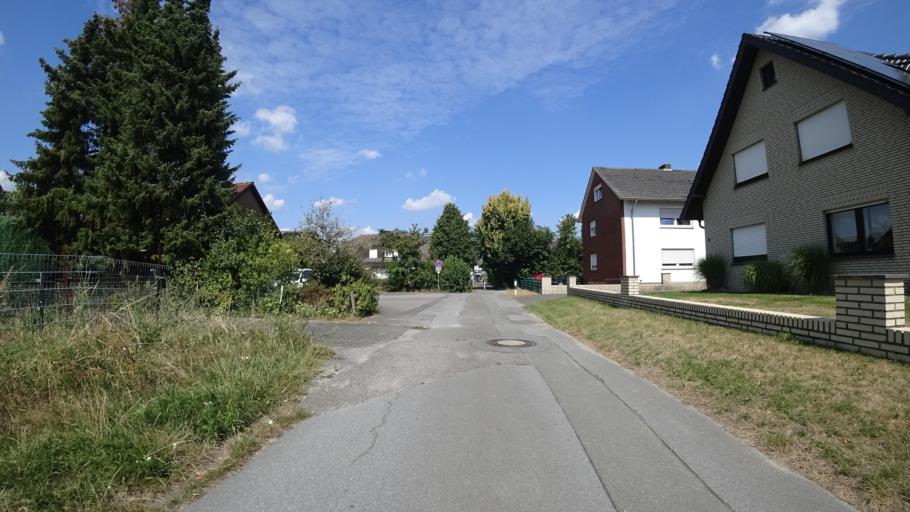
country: DE
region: North Rhine-Westphalia
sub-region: Regierungsbezirk Detmold
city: Guetersloh
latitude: 51.9139
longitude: 8.4189
